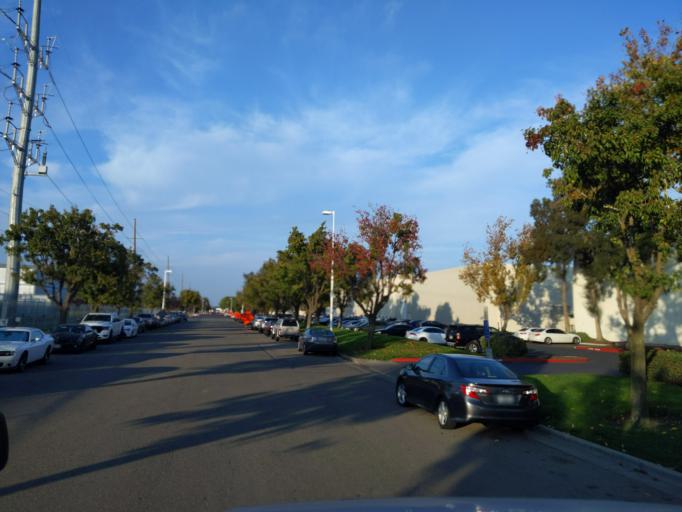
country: US
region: California
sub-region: San Joaquin County
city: Lathrop
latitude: 37.7990
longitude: -121.2939
